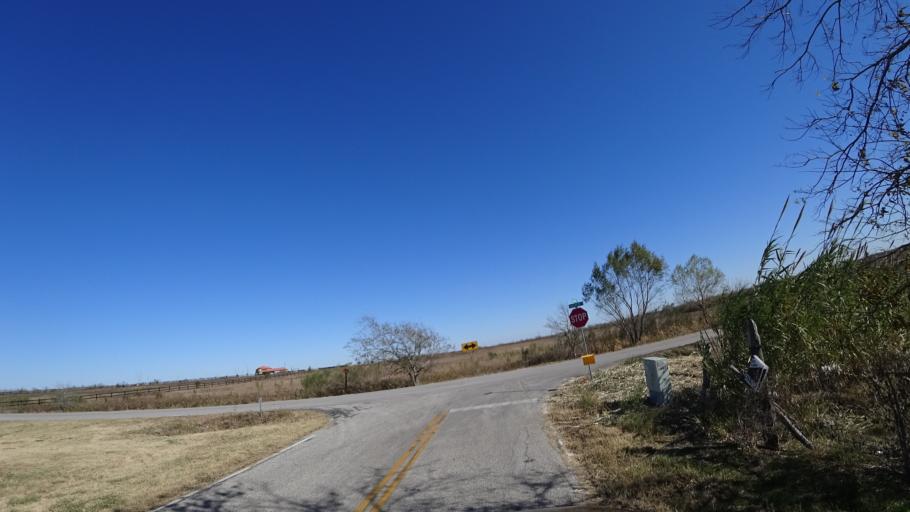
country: US
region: Texas
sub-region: Travis County
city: Garfield
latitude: 30.0991
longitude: -97.6371
